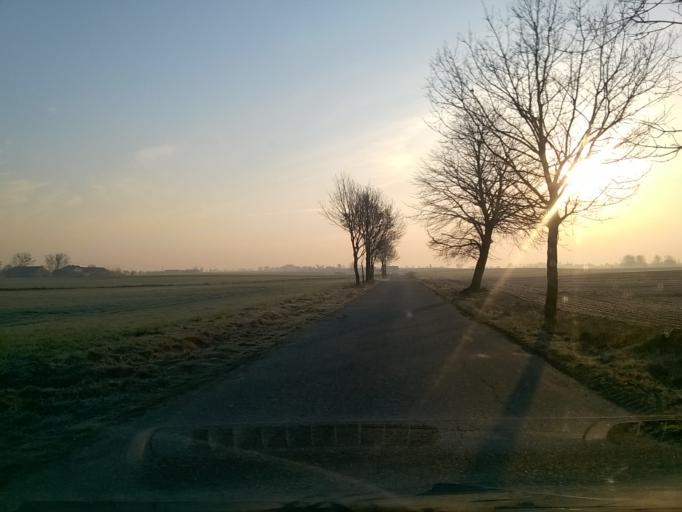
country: PL
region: Kujawsko-Pomorskie
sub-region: Powiat sepolenski
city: Sosno
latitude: 53.4489
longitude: 17.7046
